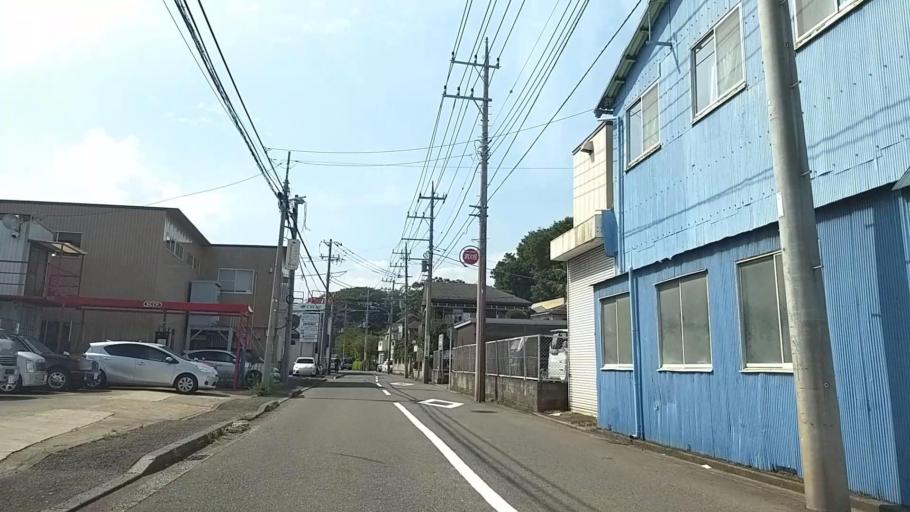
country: JP
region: Kanagawa
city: Yokohama
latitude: 35.5240
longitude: 139.5939
